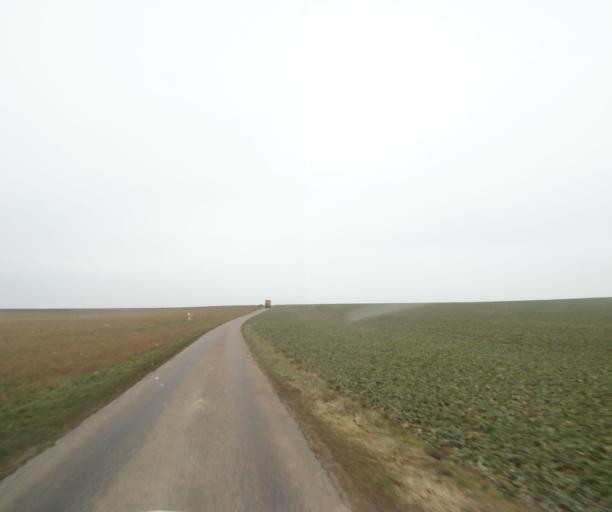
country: FR
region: Champagne-Ardenne
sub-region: Departement de la Haute-Marne
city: Chevillon
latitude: 48.5097
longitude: 5.0857
